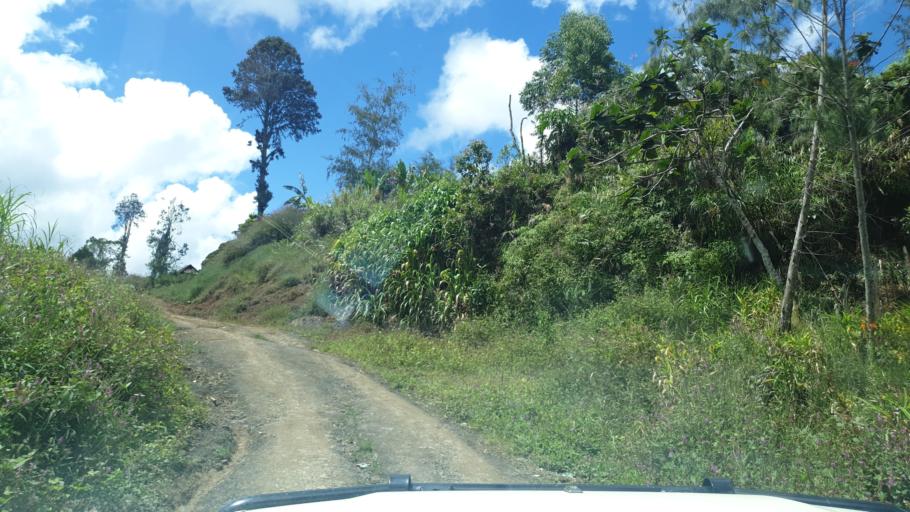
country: PG
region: Eastern Highlands
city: Goroka
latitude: -6.2766
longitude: 145.1869
